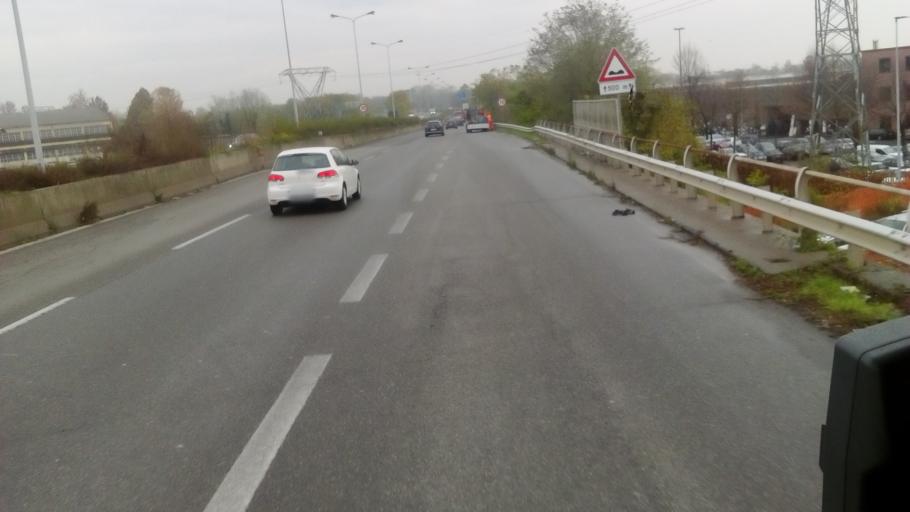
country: IT
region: Lombardy
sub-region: Provincia di Bergamo
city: Azzano San Paolo
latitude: 45.6756
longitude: 9.6725
